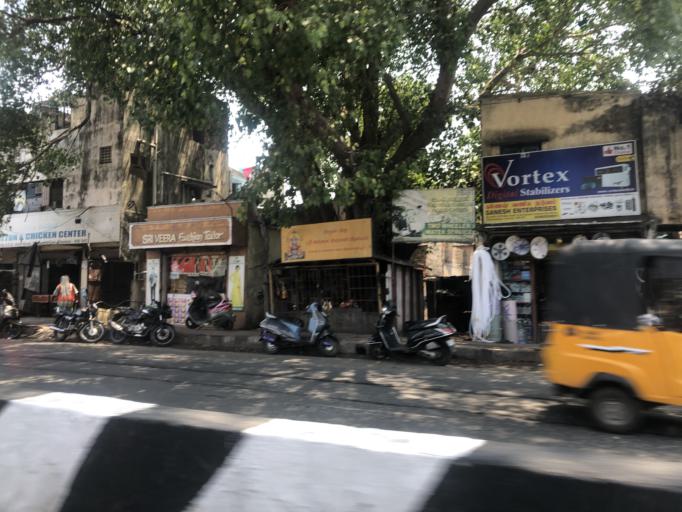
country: IN
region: Tamil Nadu
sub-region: Chennai
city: Gandhi Nagar
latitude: 12.9830
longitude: 80.2594
